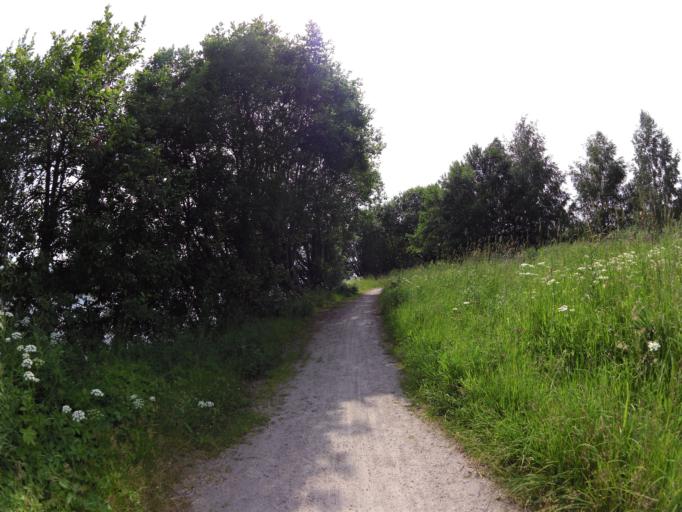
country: NO
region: Ostfold
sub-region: Fredrikstad
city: Fredrikstad
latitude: 59.2372
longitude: 10.9943
